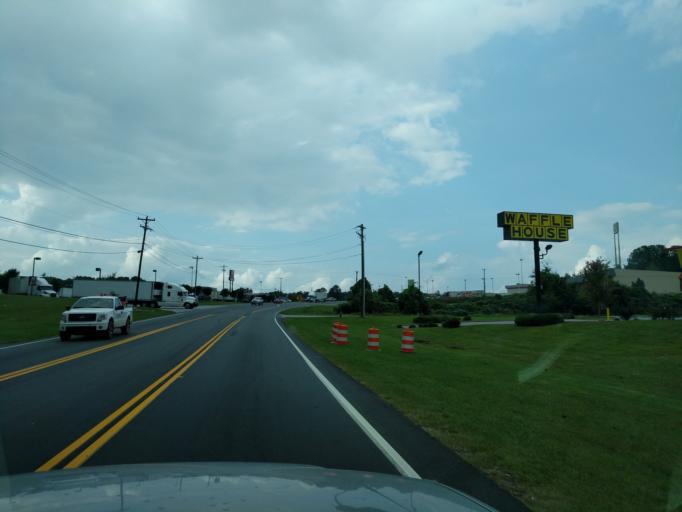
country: US
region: South Carolina
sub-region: Anderson County
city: Northlake
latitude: 34.5758
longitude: -82.6898
